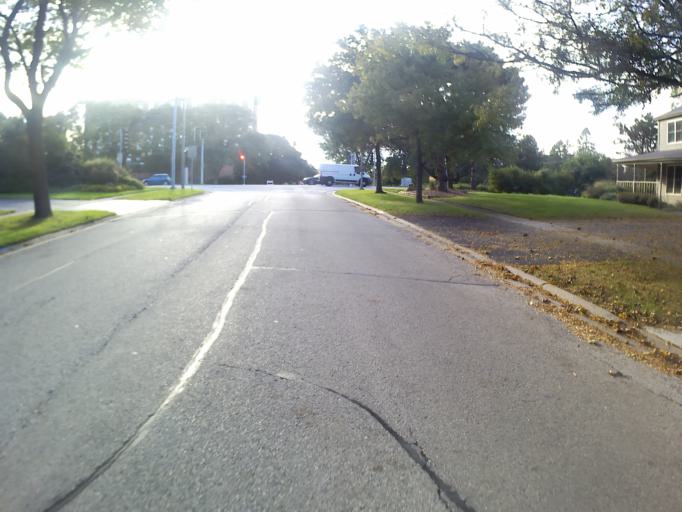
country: US
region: Illinois
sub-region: DuPage County
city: Lisle
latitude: 41.7742
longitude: -88.0699
